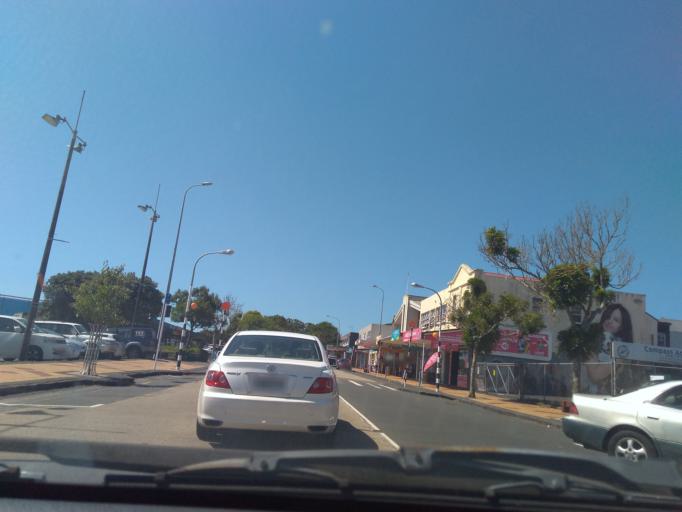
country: NZ
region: Auckland
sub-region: Auckland
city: Rosebank
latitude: -36.8980
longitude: 174.6970
